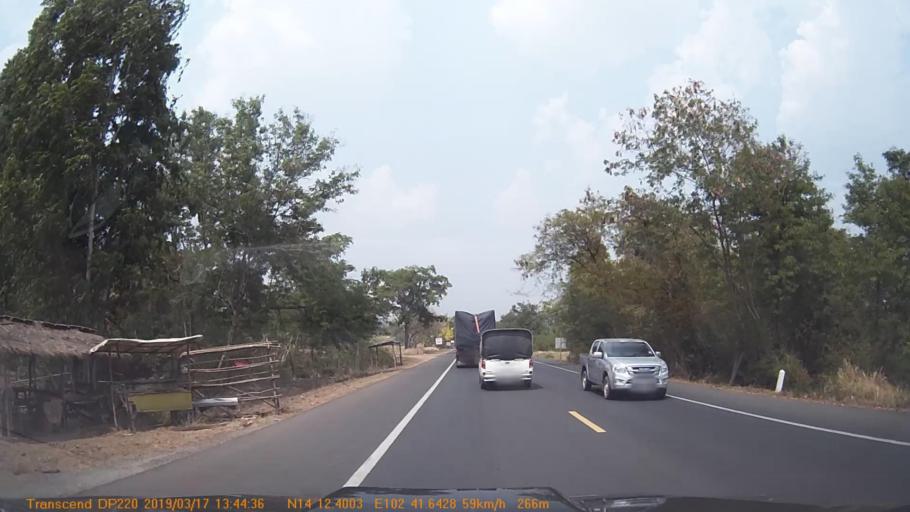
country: TH
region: Buriram
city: Non Din Daeng
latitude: 14.2069
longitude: 102.6941
